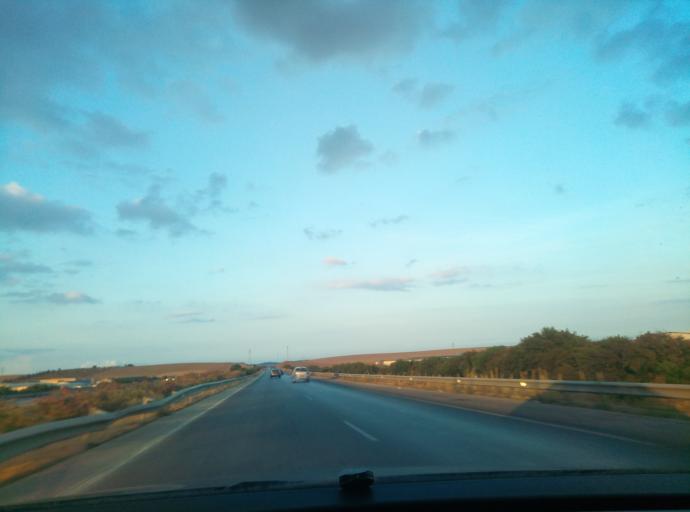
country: TN
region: Tunis
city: Oued Lill
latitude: 36.7248
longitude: 9.9936
